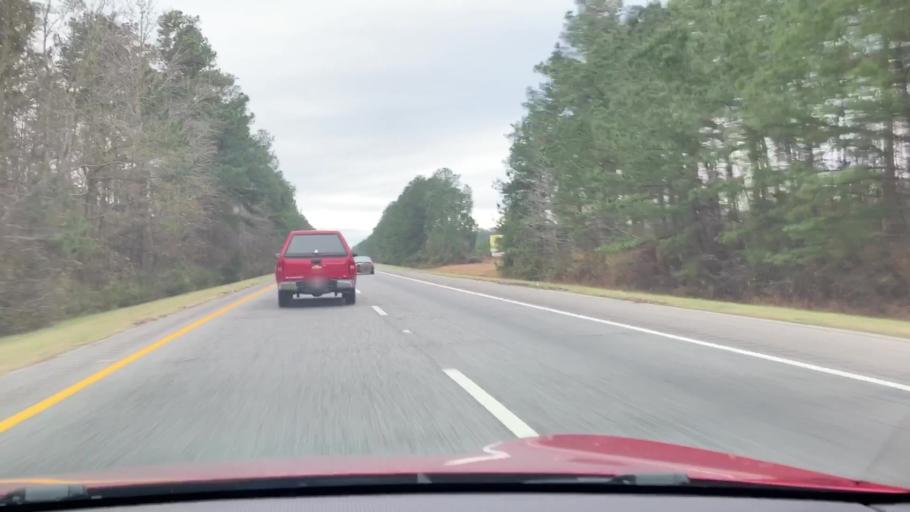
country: US
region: South Carolina
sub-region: Clarendon County
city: Manning
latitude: 33.6769
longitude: -80.2652
